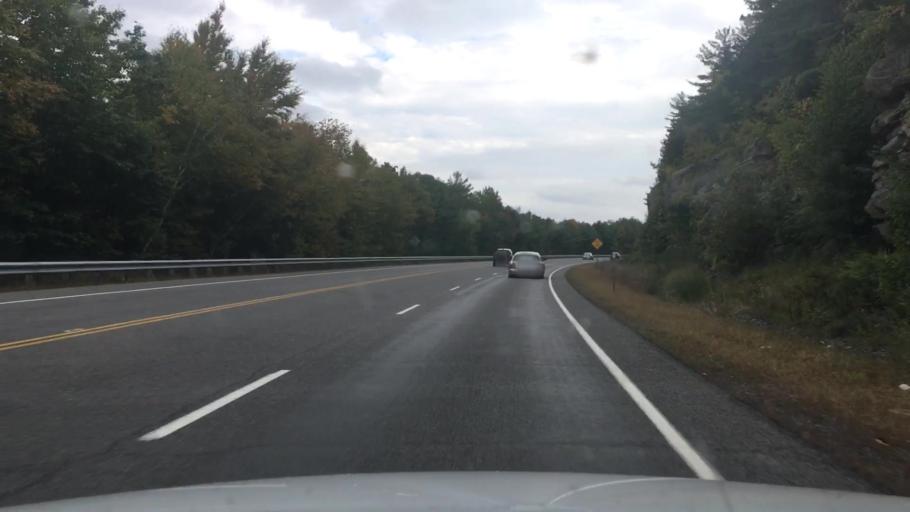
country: US
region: New Hampshire
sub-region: Carroll County
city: Wolfeboro
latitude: 43.5354
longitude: -71.2786
